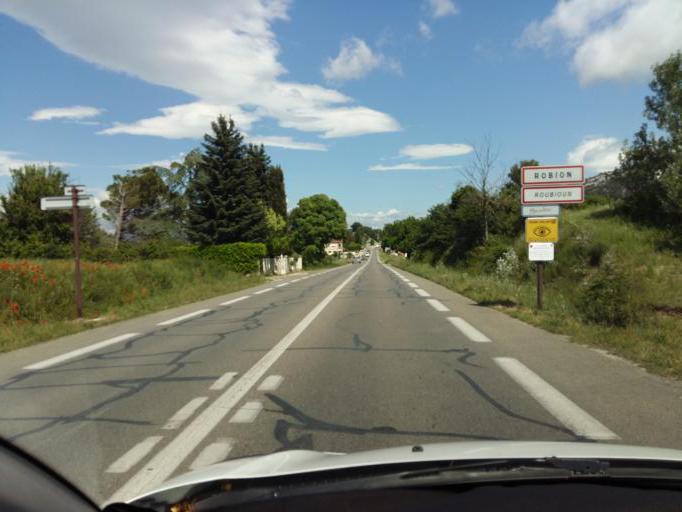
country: FR
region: Provence-Alpes-Cote d'Azur
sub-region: Departement du Vaucluse
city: Taillades
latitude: 43.8458
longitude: 5.0980
